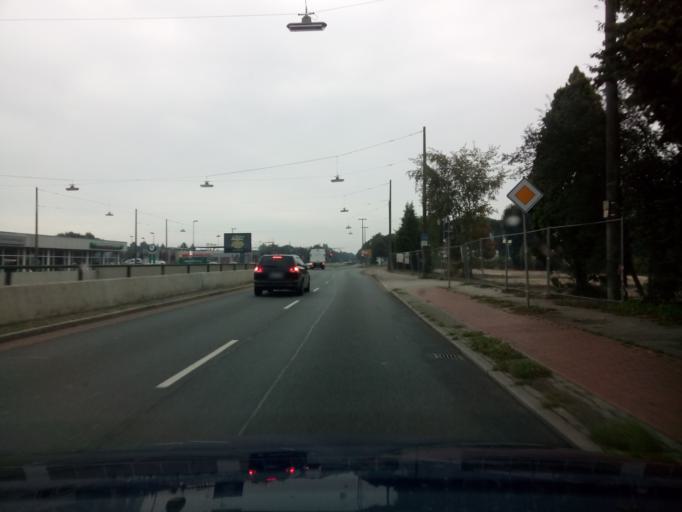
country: DE
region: Bremen
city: Bremen
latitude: 53.0489
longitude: 8.8169
